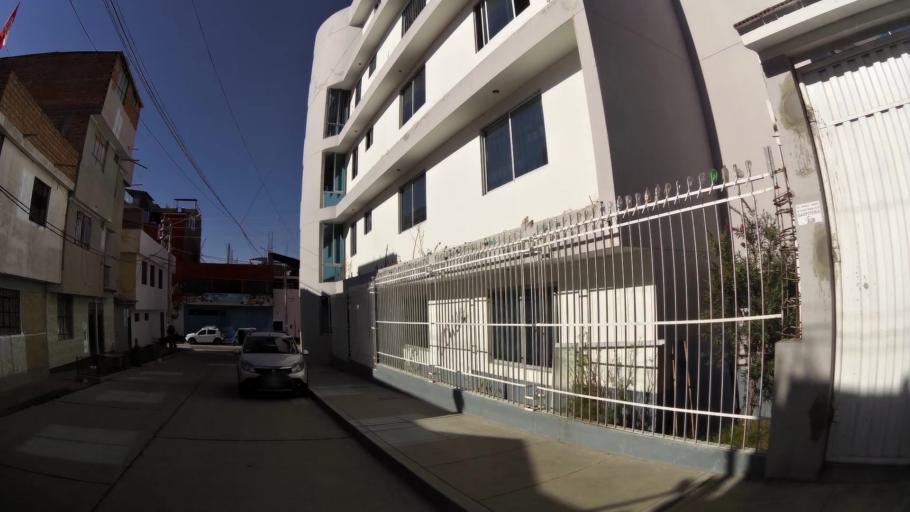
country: PE
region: Ayacucho
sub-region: Provincia de Huamanga
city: Ayacucho
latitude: -13.1501
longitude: -74.2273
